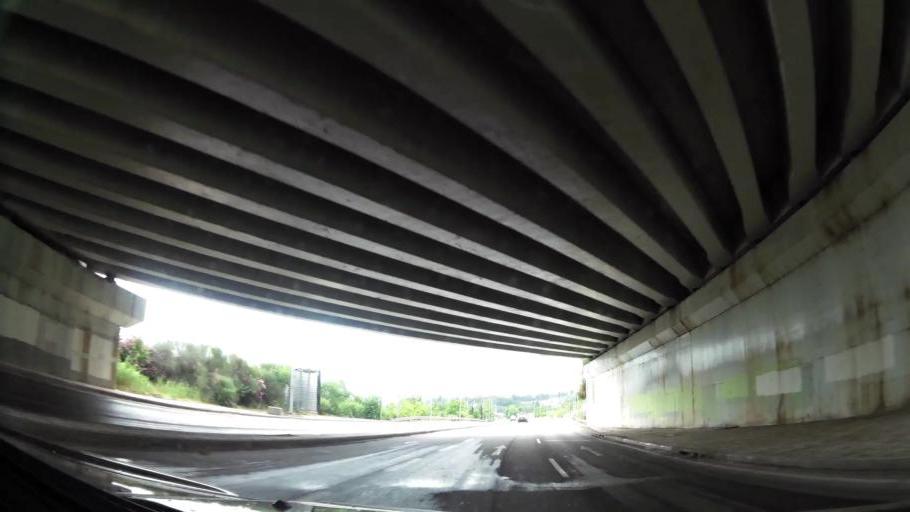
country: GR
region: Central Macedonia
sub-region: Nomos Imathias
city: Veroia
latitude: 40.5054
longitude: 22.2294
